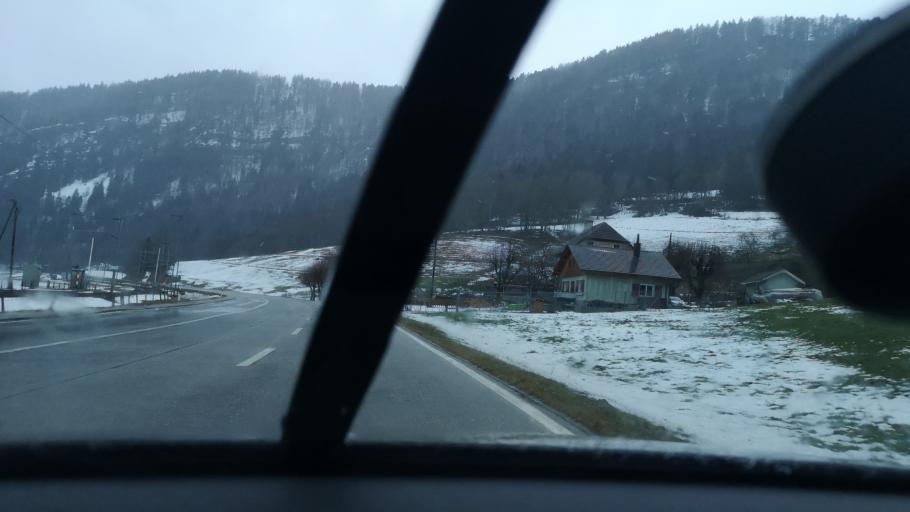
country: CH
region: Neuchatel
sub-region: Val-de-Travers District
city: Travers
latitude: 46.9573
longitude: 6.7042
